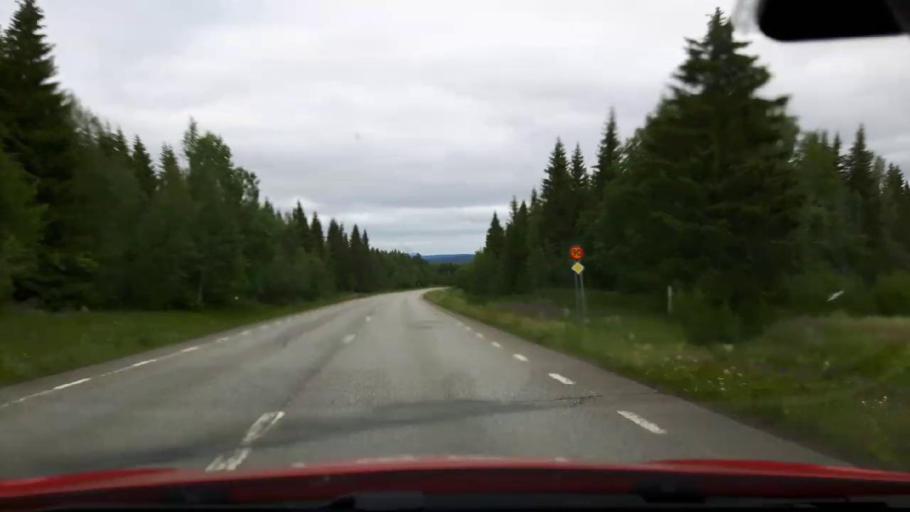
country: SE
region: Jaemtland
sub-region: Krokoms Kommun
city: Krokom
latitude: 63.5848
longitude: 14.6358
